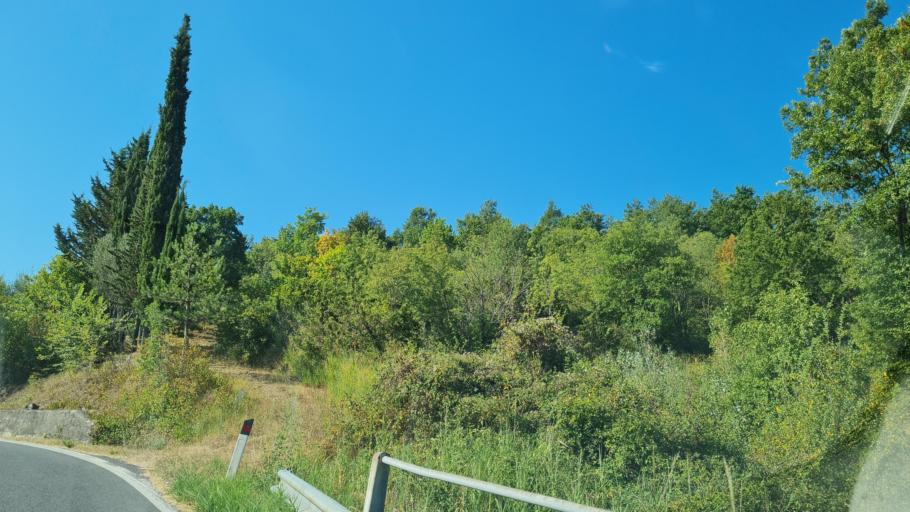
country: IT
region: Tuscany
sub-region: Provincia di Siena
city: Abbadia San Salvatore
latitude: 42.9340
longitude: 11.7013
